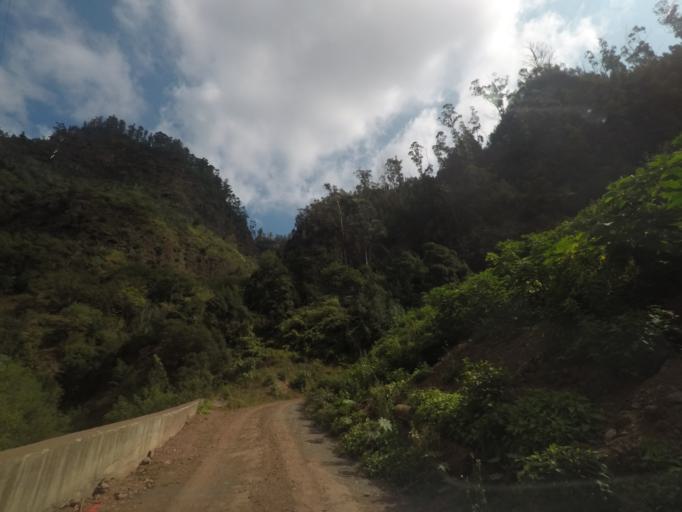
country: PT
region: Madeira
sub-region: Funchal
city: Nossa Senhora do Monte
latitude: 32.6861
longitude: -16.9152
